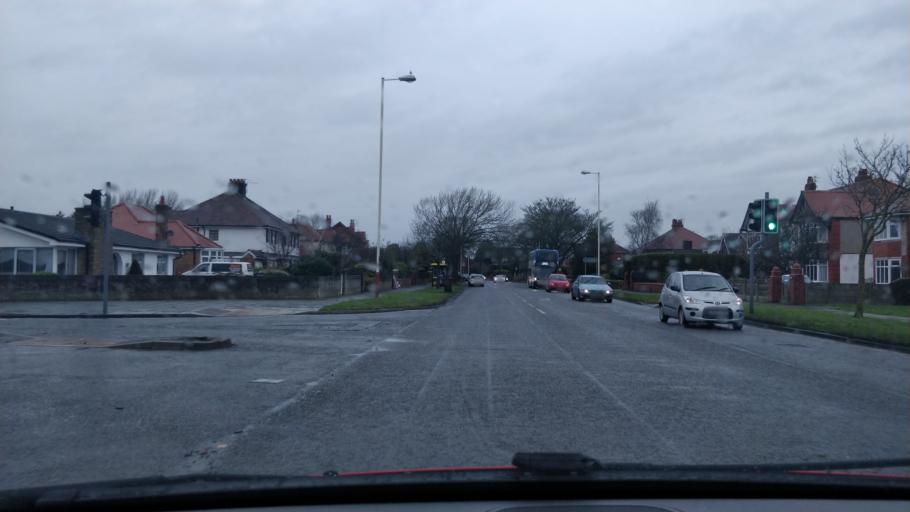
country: GB
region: England
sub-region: Sefton
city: Formby
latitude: 53.5968
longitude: -3.0365
